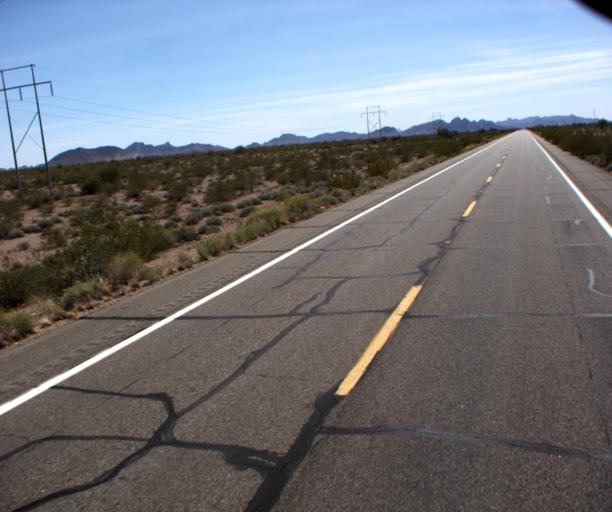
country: US
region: Arizona
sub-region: La Paz County
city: Quartzsite
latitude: 33.3954
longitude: -114.2172
